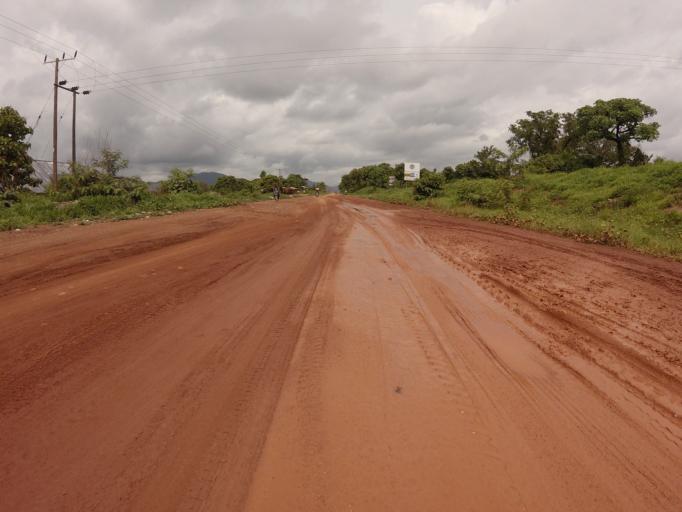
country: TG
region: Centrale
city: Sotouboua
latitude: 8.2768
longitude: 0.5099
